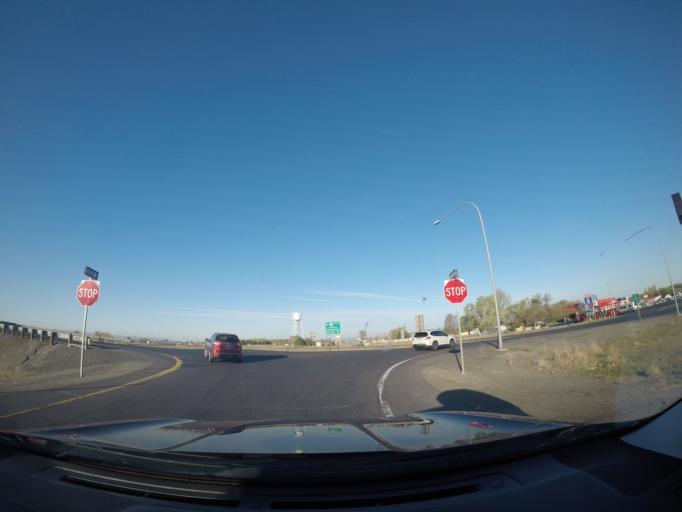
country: US
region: Washington
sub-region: Grant County
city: Quincy
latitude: 47.0837
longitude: -119.8608
